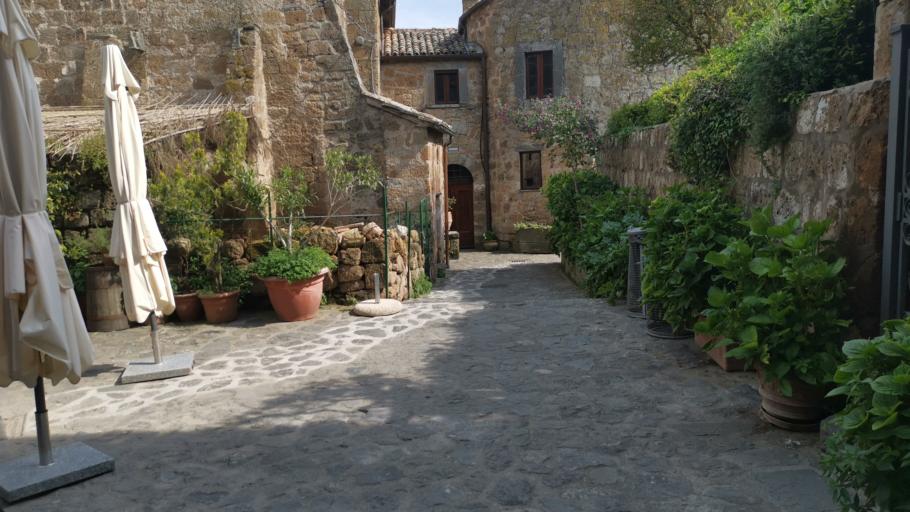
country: IT
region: Latium
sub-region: Provincia di Viterbo
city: Lubriano
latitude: 42.6275
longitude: 12.1139
